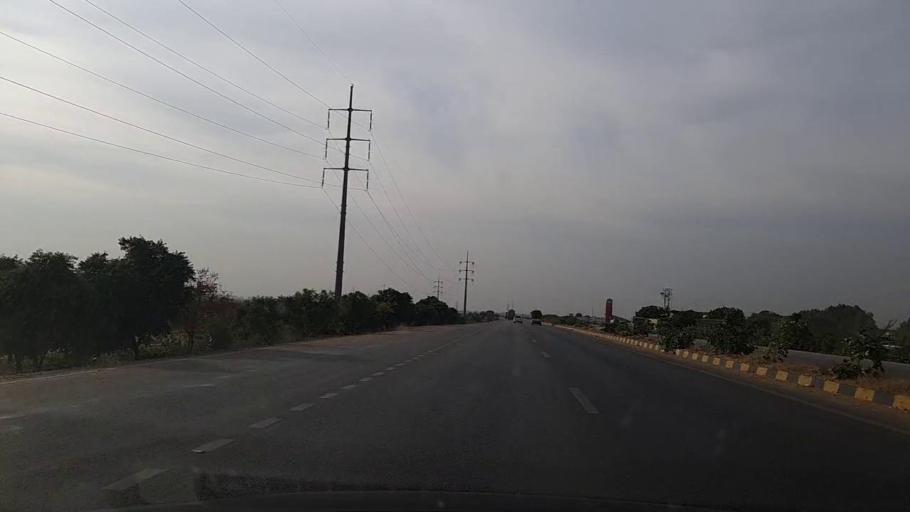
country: PK
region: Sindh
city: Gharo
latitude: 24.8348
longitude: 67.4563
